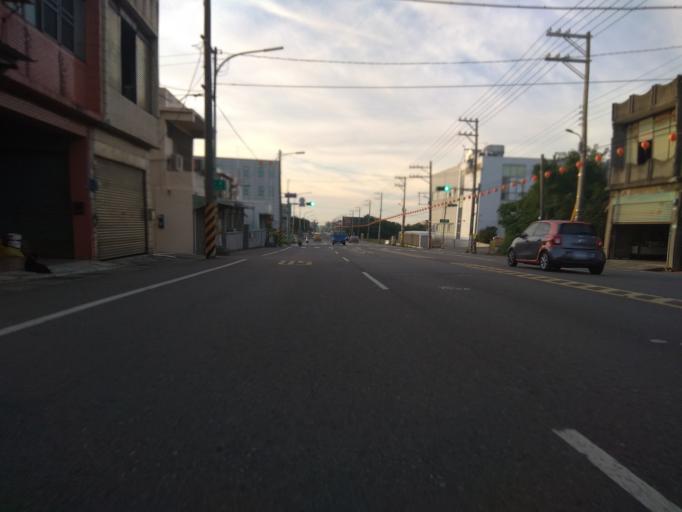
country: TW
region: Taiwan
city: Taoyuan City
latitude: 24.9991
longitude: 121.1588
